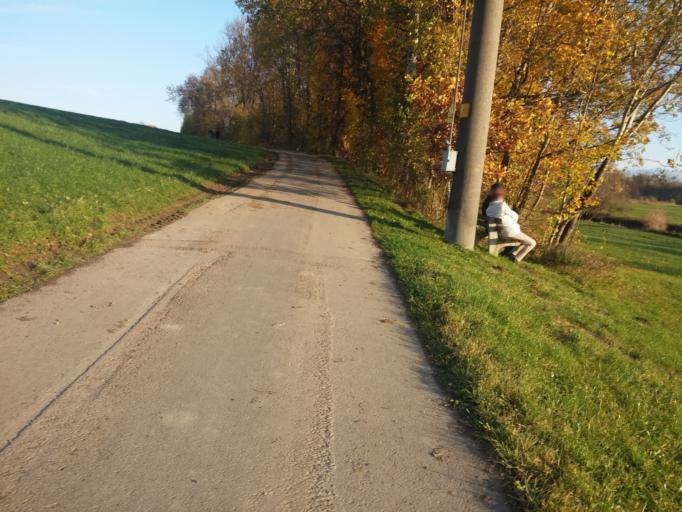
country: DE
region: Bavaria
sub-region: Upper Bavaria
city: Bad Aibling
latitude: 47.8782
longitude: 12.0025
